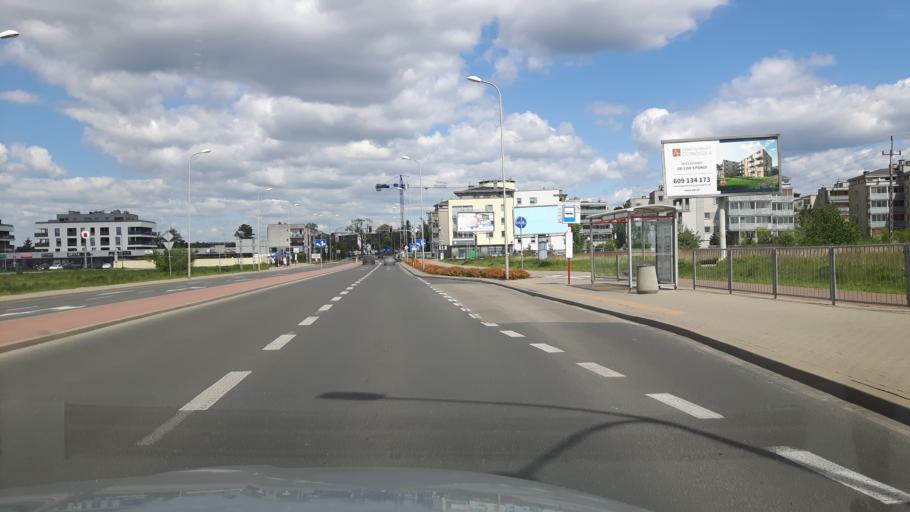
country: PL
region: Masovian Voivodeship
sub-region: Warszawa
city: Targowek
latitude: 52.3103
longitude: 21.0625
